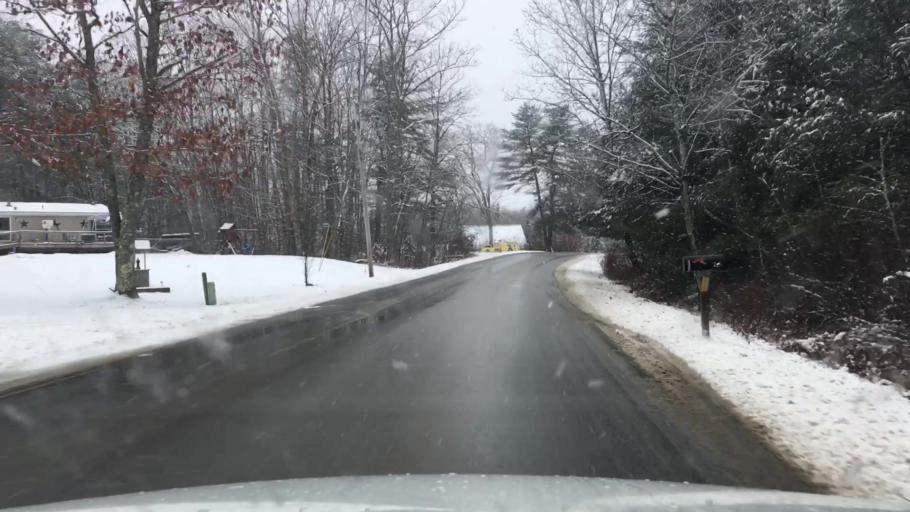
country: US
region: Maine
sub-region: Knox County
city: Union
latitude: 44.1580
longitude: -69.2964
